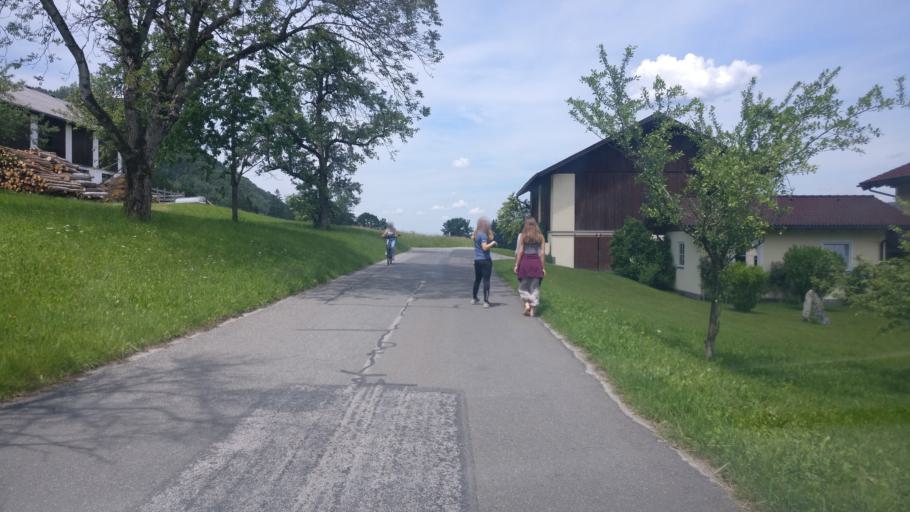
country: AT
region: Salzburg
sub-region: Politischer Bezirk Hallein
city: Kuchl
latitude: 47.6347
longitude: 13.1288
